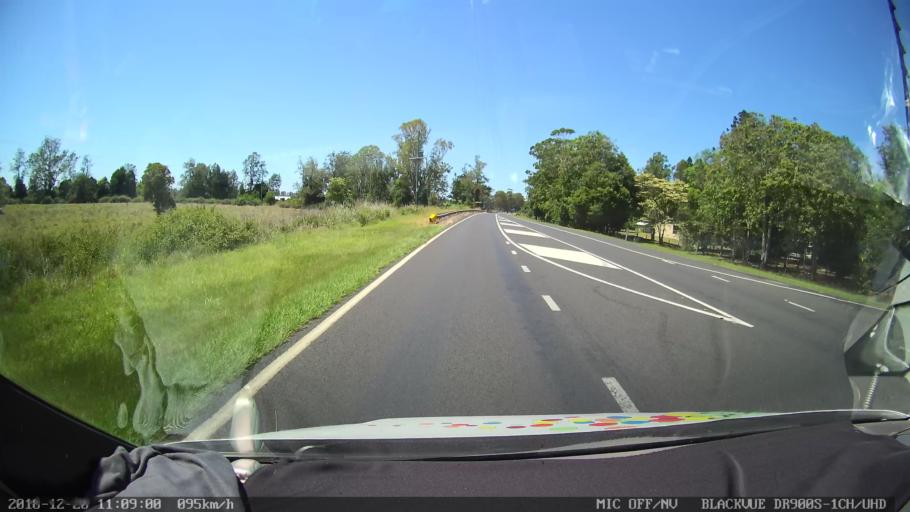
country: AU
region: New South Wales
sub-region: Richmond Valley
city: Casino
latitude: -28.9300
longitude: 153.0047
